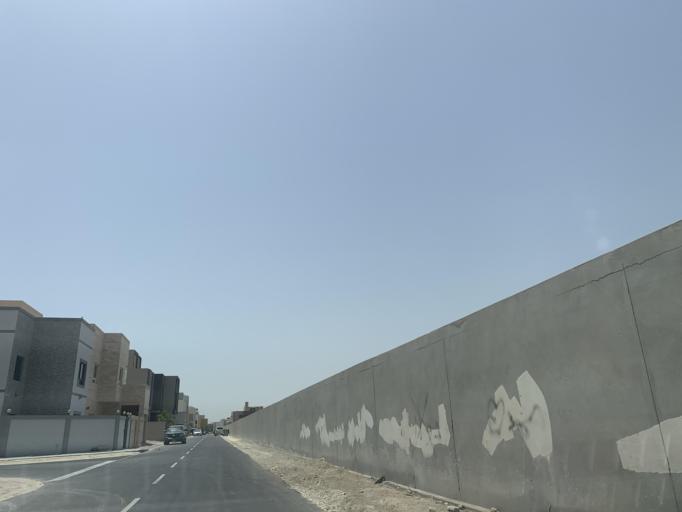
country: BH
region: Northern
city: Madinat `Isa
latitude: 26.1615
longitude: 50.5785
